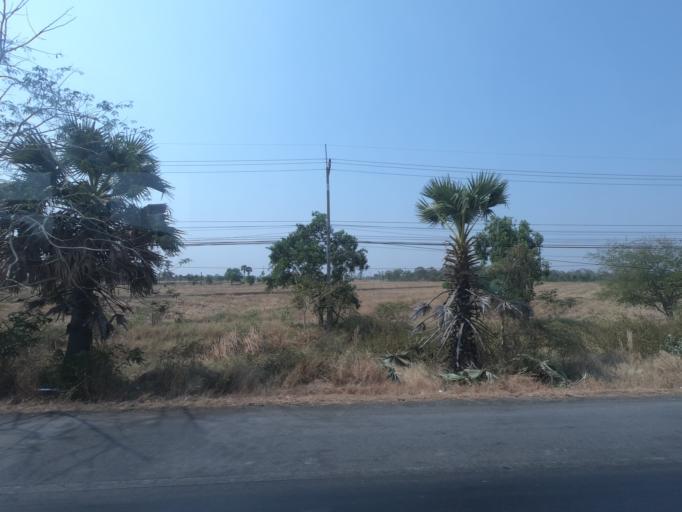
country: TH
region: Nakhon Ratchasima
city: Non Sung
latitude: 15.1604
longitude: 102.3305
